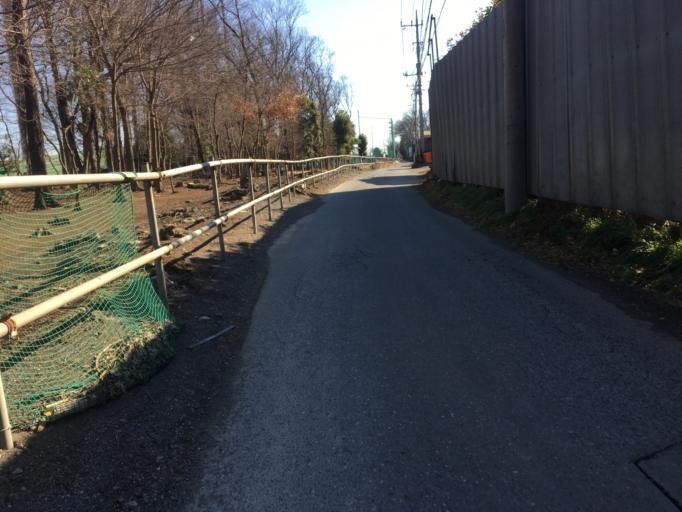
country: JP
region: Saitama
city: Oi
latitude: 35.8234
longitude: 139.5299
